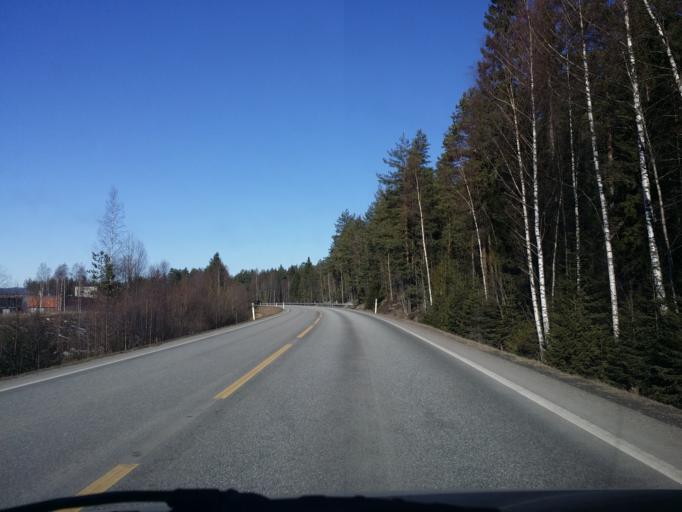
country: NO
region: Buskerud
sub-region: Ringerike
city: Honefoss
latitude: 60.2239
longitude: 10.2549
